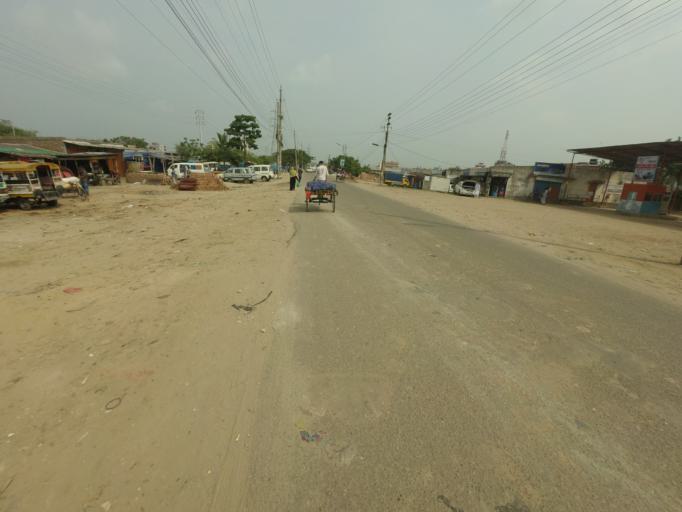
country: BD
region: Dhaka
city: Azimpur
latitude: 23.7285
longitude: 90.3660
